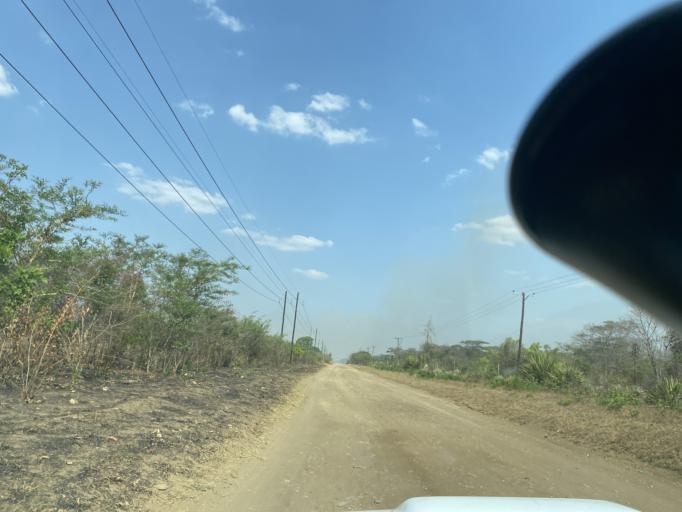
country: ZM
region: Lusaka
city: Lusaka
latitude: -15.3022
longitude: 28.0316
